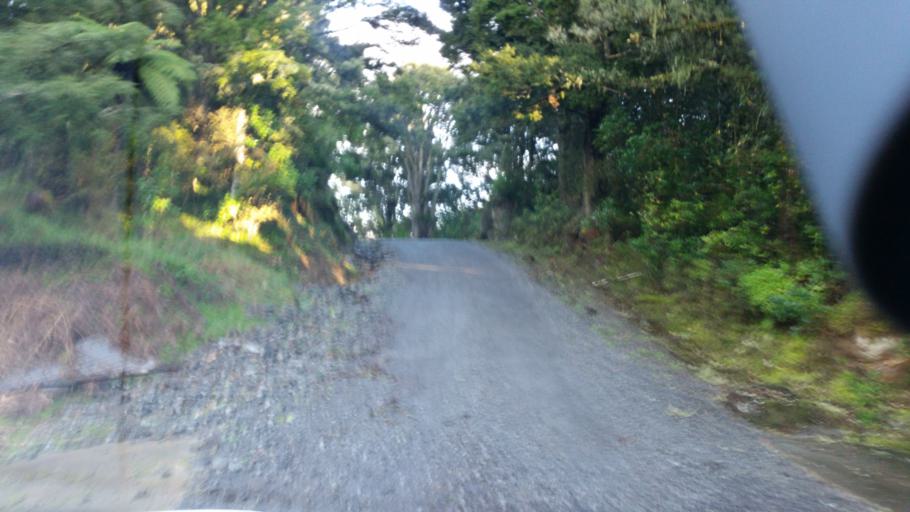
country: NZ
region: Northland
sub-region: Whangarei
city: Maungatapere
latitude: -35.7774
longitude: 174.1061
